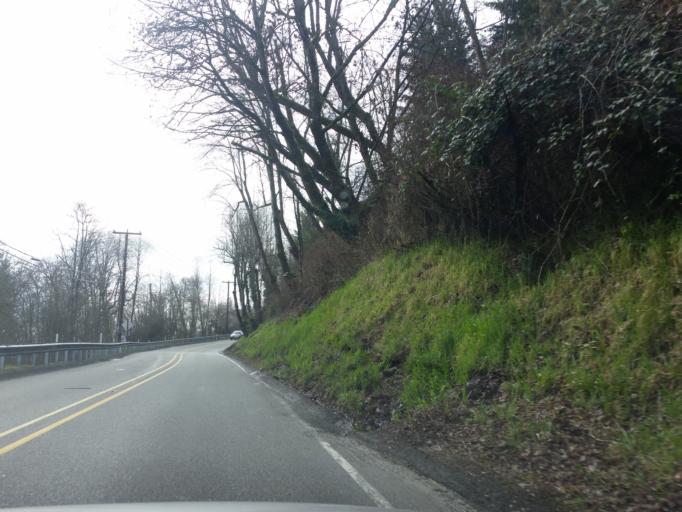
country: US
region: Washington
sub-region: Pierce County
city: McMillin
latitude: 47.1482
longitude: -122.2420
